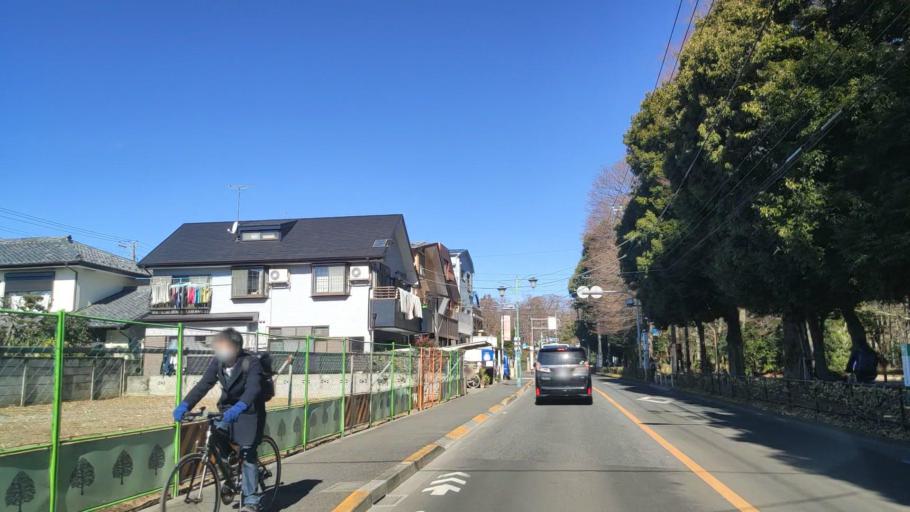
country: JP
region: Tokyo
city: Musashino
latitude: 35.6978
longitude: 139.5701
